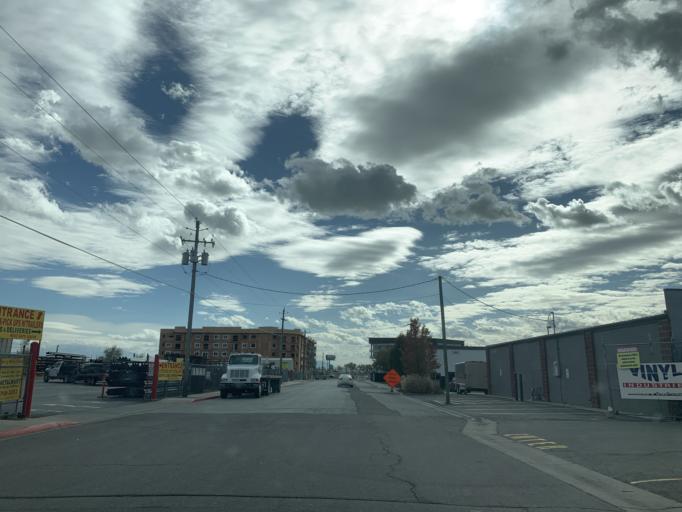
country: US
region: Utah
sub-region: Utah County
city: Lehi
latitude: 40.3873
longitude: -111.8291
